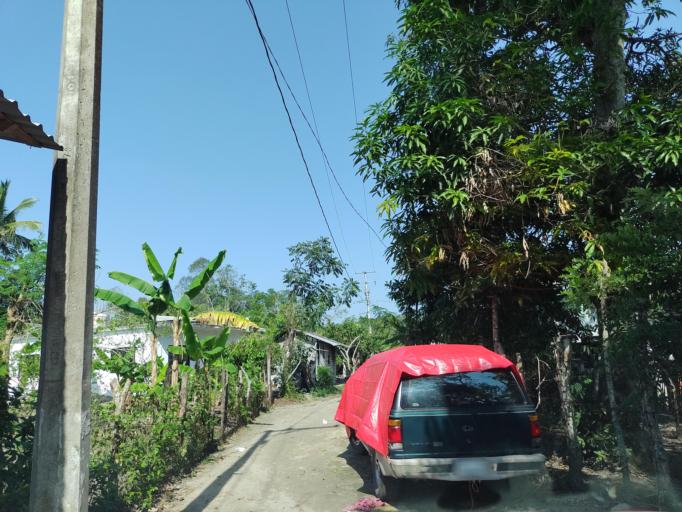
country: MX
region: Veracruz
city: Agua Dulce
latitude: 20.2570
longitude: -97.2509
